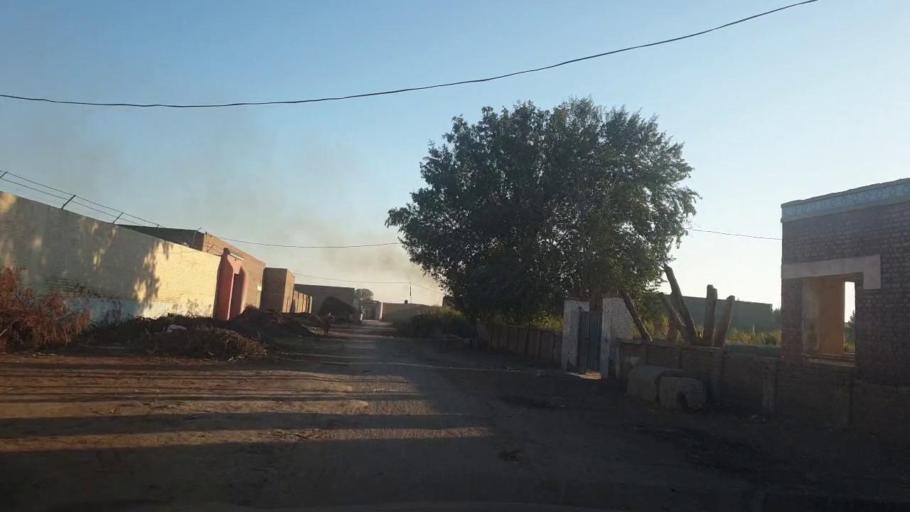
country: PK
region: Sindh
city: Ghotki
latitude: 27.9951
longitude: 69.2832
